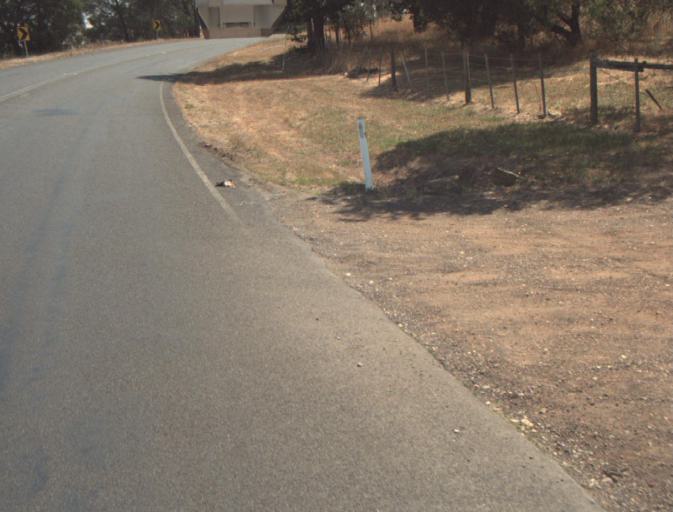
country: AU
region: Tasmania
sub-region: Launceston
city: Summerhill
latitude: -41.4990
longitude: 147.1716
